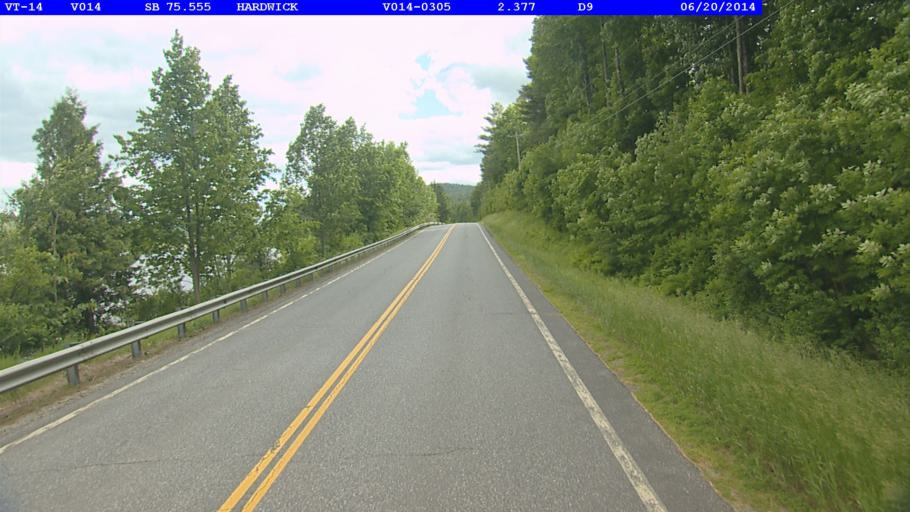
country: US
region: Vermont
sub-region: Caledonia County
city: Hardwick
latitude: 44.5284
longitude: -72.3744
